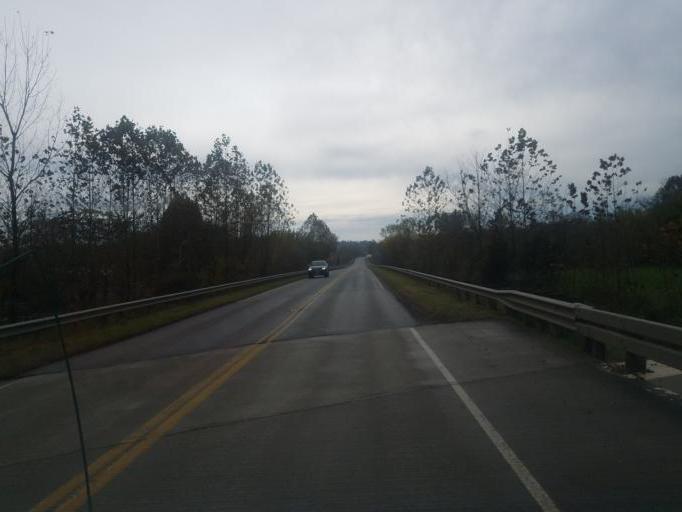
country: US
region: Ohio
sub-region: Washington County
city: Beverly
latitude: 39.5484
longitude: -81.6473
